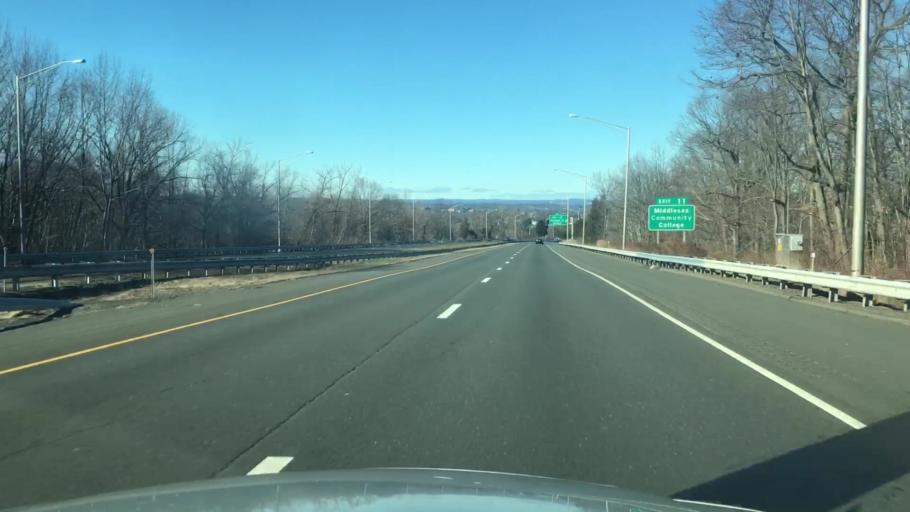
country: US
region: Connecticut
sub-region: Middlesex County
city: Middletown
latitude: 41.5279
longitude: -72.6131
